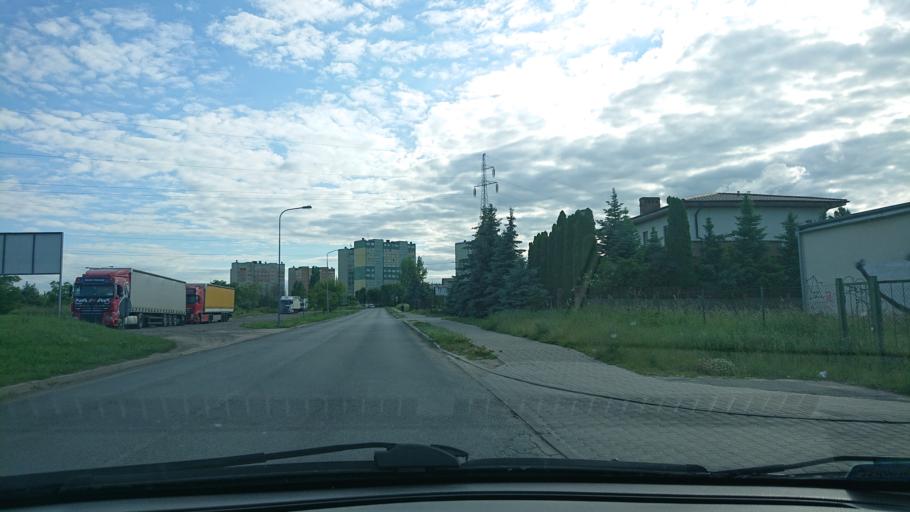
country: PL
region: Greater Poland Voivodeship
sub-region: Powiat gnieznienski
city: Gniezno
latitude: 52.5524
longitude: 17.6164
